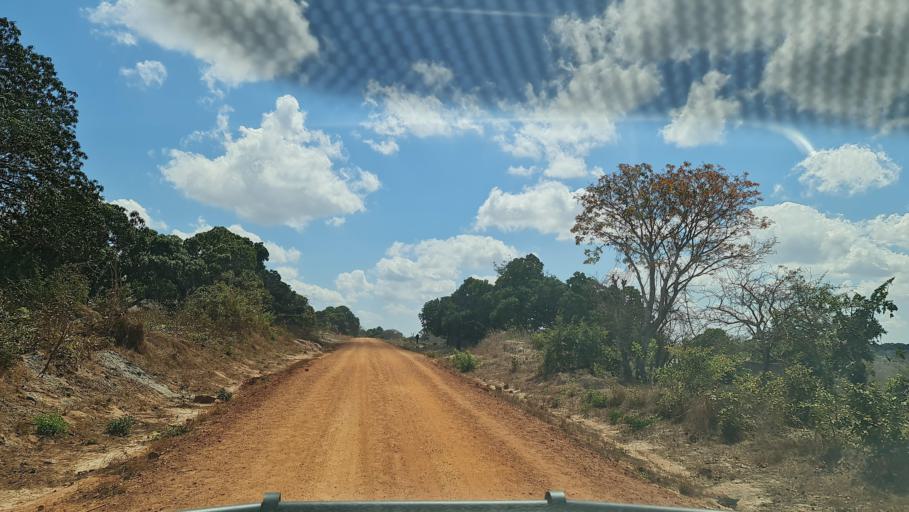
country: MZ
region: Nampula
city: Nacala
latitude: -14.1712
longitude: 40.2453
